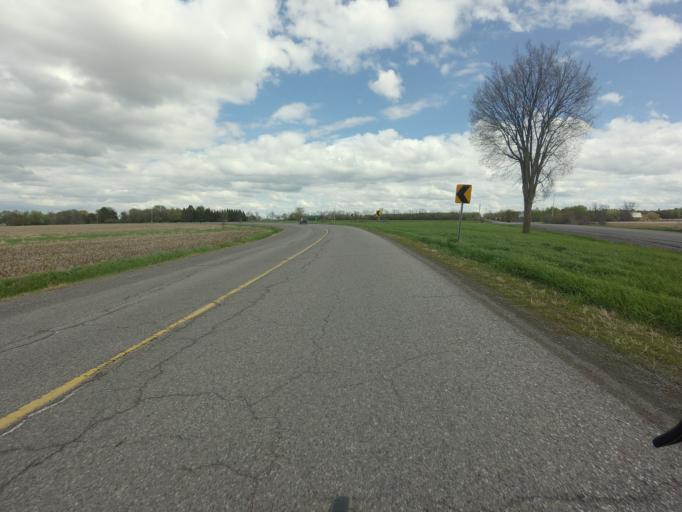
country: CA
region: Ontario
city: Carleton Place
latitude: 45.3312
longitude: -76.0890
